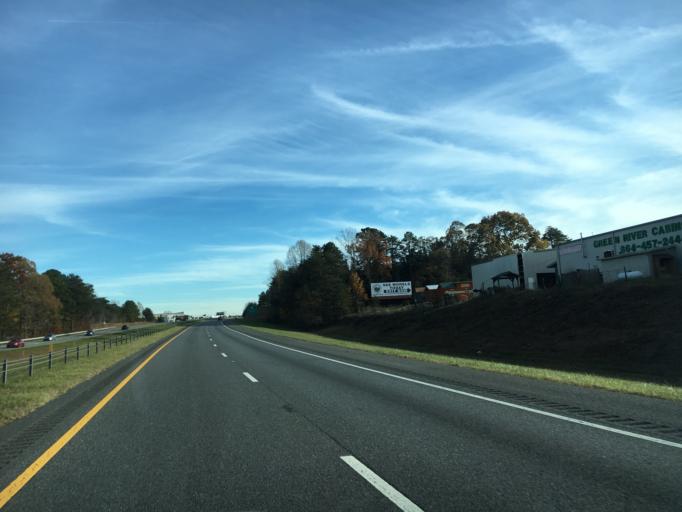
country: US
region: South Carolina
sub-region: Spartanburg County
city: Landrum
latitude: 35.1538
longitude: -82.1174
